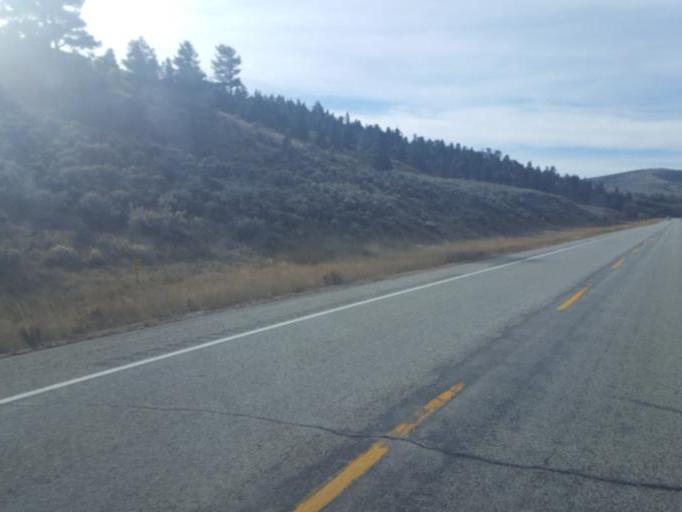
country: US
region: Colorado
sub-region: Costilla County
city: San Luis
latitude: 37.5260
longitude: -105.2980
